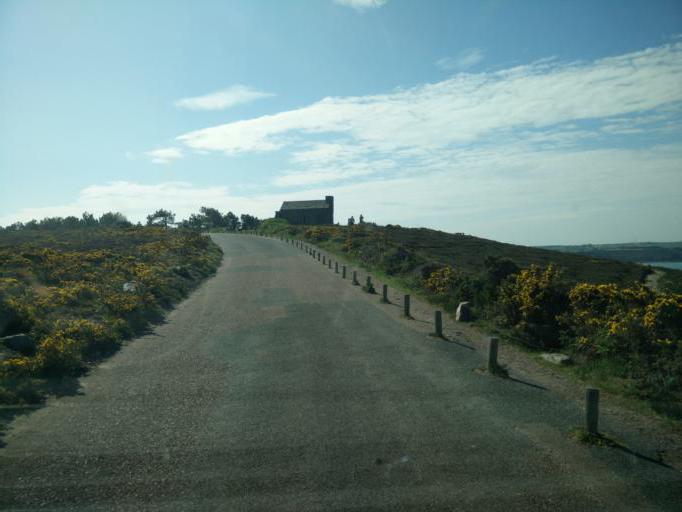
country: FR
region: Brittany
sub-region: Departement des Cotes-d'Armor
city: Erquy
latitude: 48.6402
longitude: -2.4818
